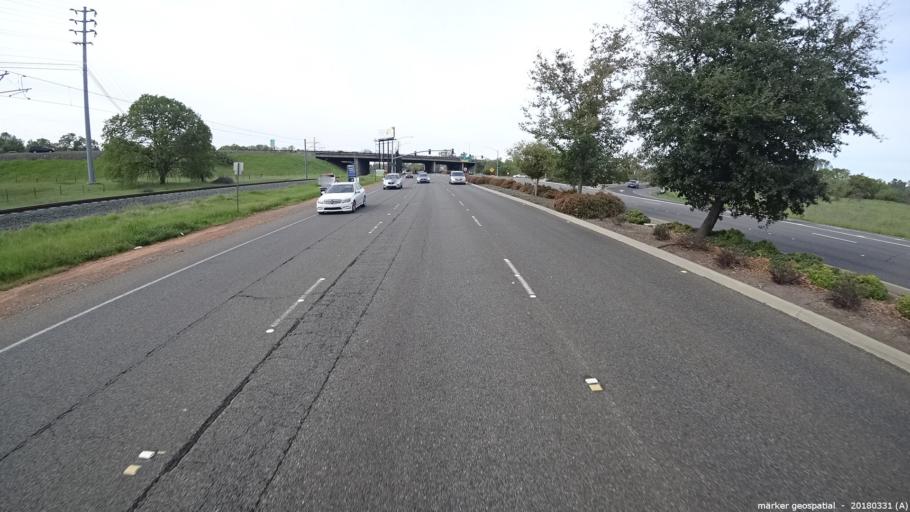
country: US
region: California
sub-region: Sacramento County
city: Folsom
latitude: 38.6413
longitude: -121.1953
